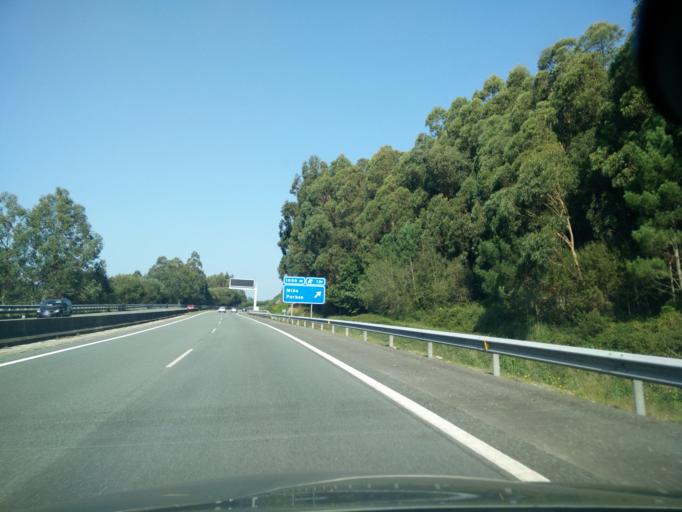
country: ES
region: Galicia
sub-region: Provincia da Coruna
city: Mino
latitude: 43.3394
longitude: -8.1992
